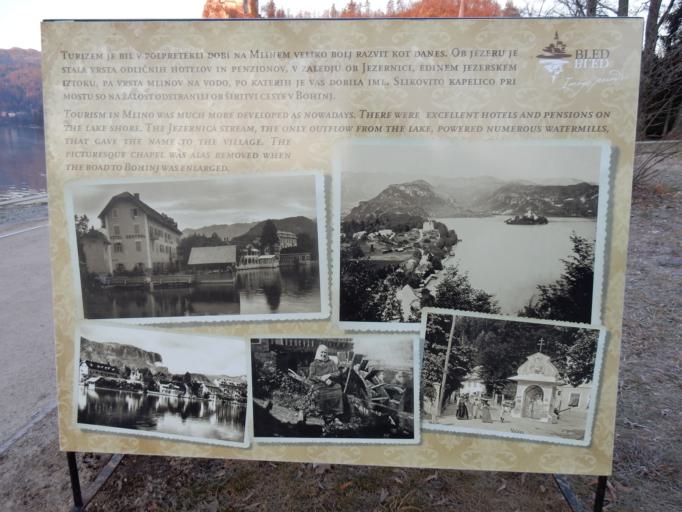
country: SI
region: Bled
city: Bled
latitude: 46.3689
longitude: 14.1077
